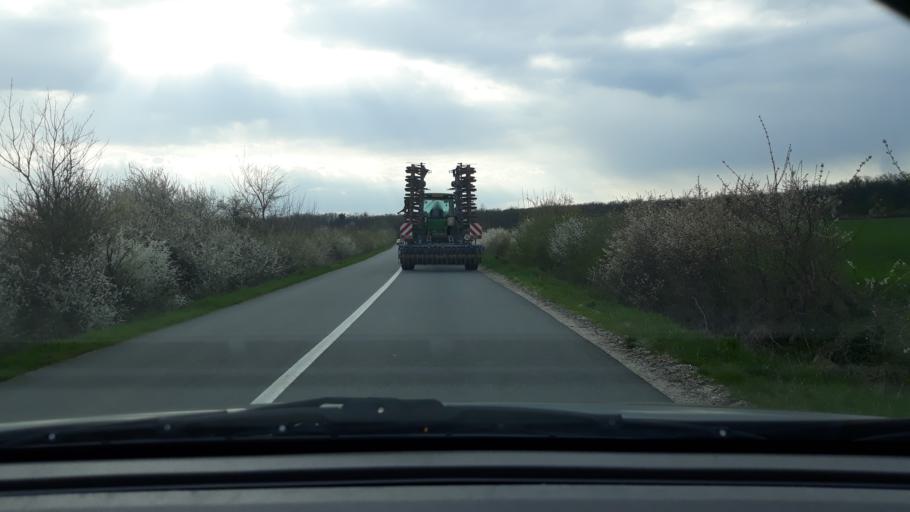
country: RO
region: Bihor
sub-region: Comuna Buduslau
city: Albis
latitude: 47.3581
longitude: 22.2145
